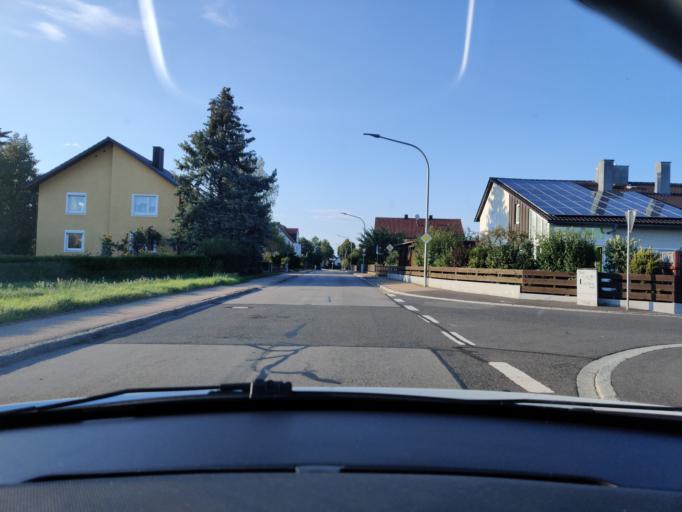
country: DE
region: Bavaria
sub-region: Upper Palatinate
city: Nabburg
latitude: 49.4481
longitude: 12.1940
